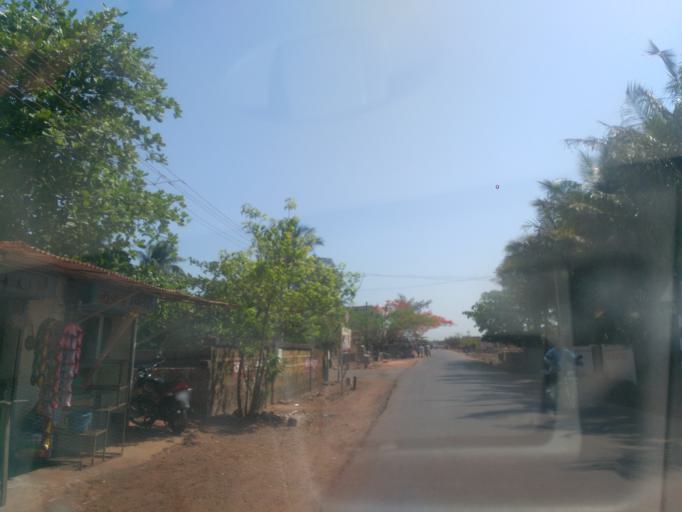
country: IN
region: Maharashtra
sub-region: Ratnagiri
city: Makhjan
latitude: 17.2386
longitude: 73.2709
